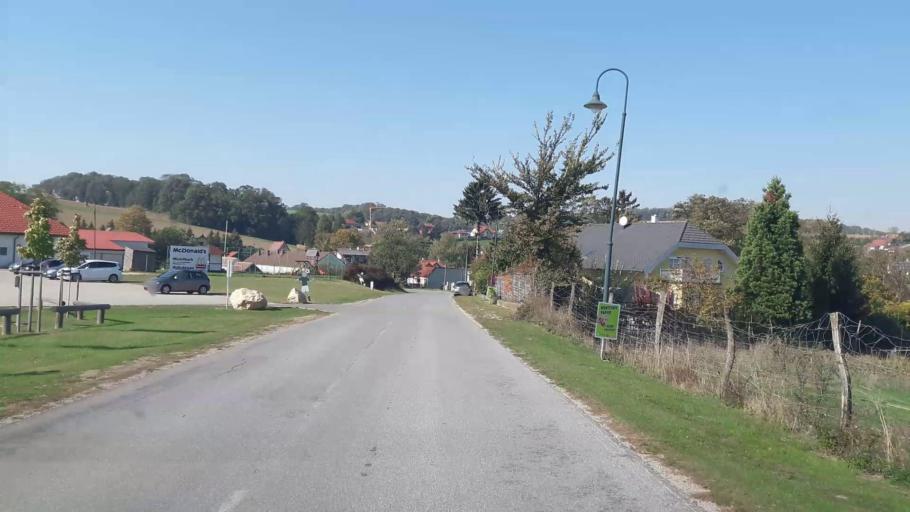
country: AT
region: Lower Austria
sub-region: Politischer Bezirk Korneuburg
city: Ernstbrunn
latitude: 48.5212
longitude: 16.3605
